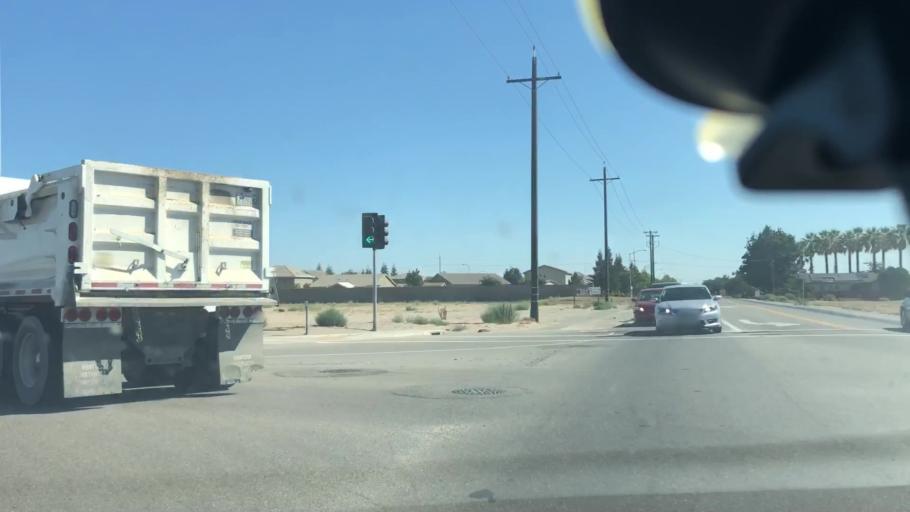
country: US
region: California
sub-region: San Joaquin County
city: Manteca
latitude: 37.7793
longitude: -121.2157
